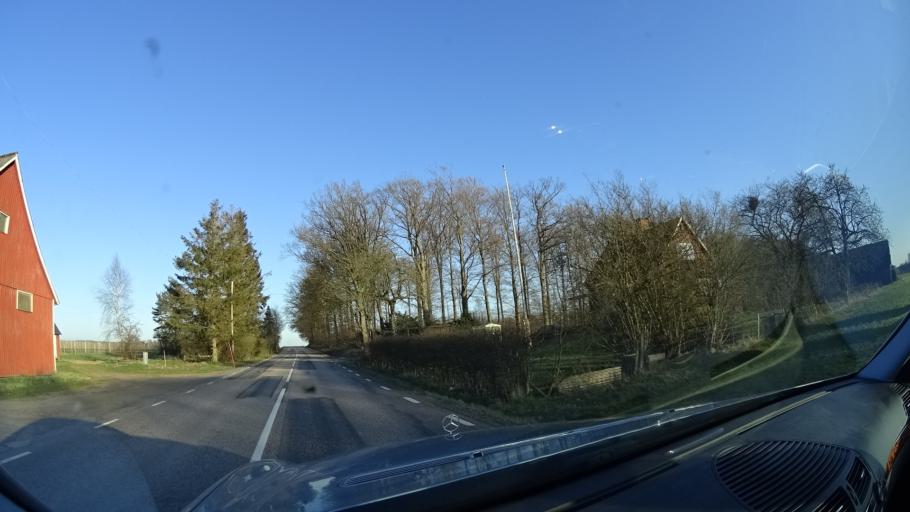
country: SE
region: Skane
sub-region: Bjuvs Kommun
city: Billesholm
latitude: 56.0327
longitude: 13.0323
